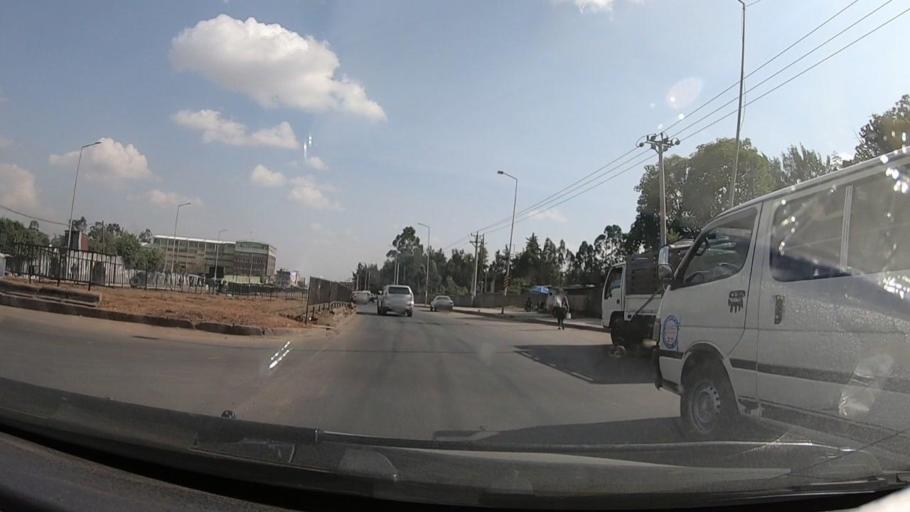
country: ET
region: Adis Abeba
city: Addis Ababa
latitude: 8.9855
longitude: 38.6945
